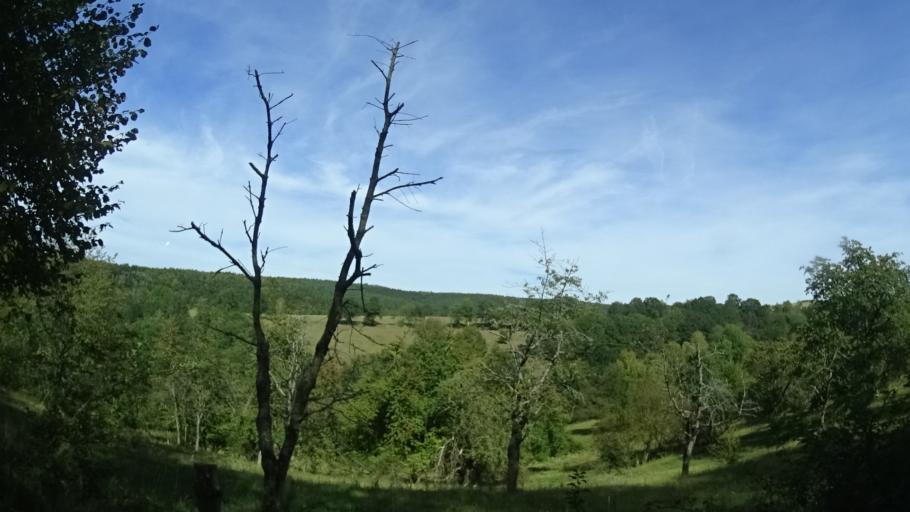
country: DE
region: Thuringia
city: Metzels
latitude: 50.6529
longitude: 10.4218
